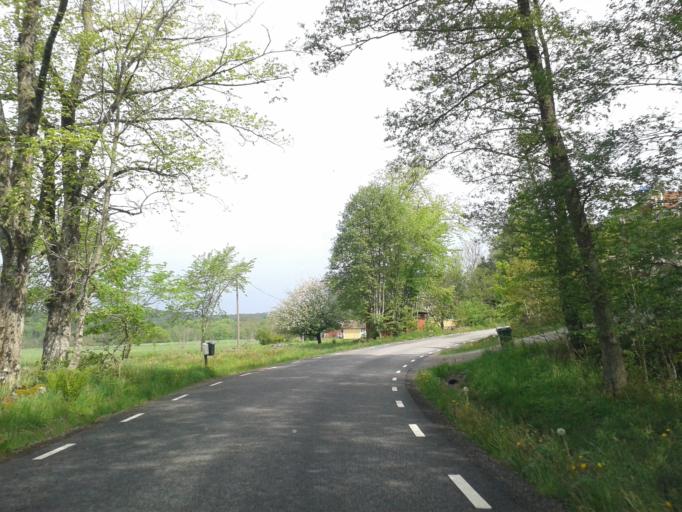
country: SE
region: Vaestra Goetaland
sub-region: Kungalvs Kommun
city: Kungalv
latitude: 57.9127
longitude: 11.9469
